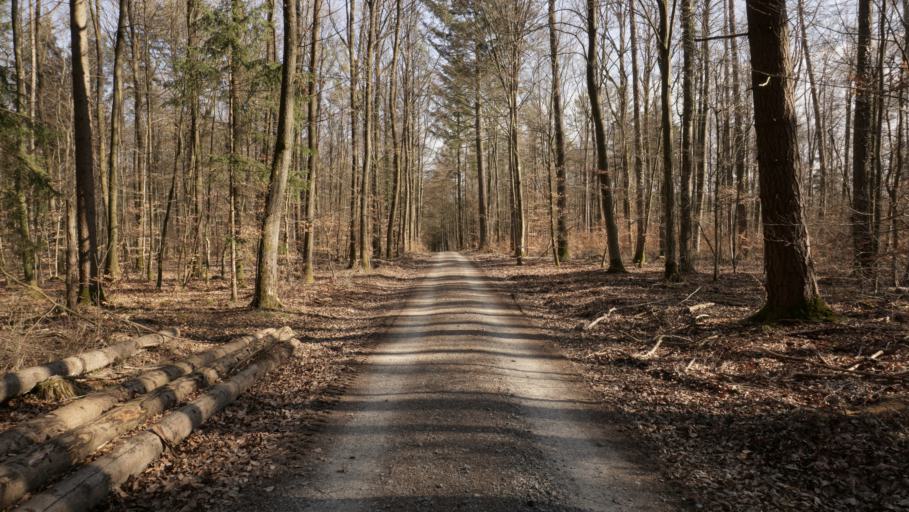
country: DE
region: Baden-Wuerttemberg
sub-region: Karlsruhe Region
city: Mosbach
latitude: 49.3882
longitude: 9.1704
